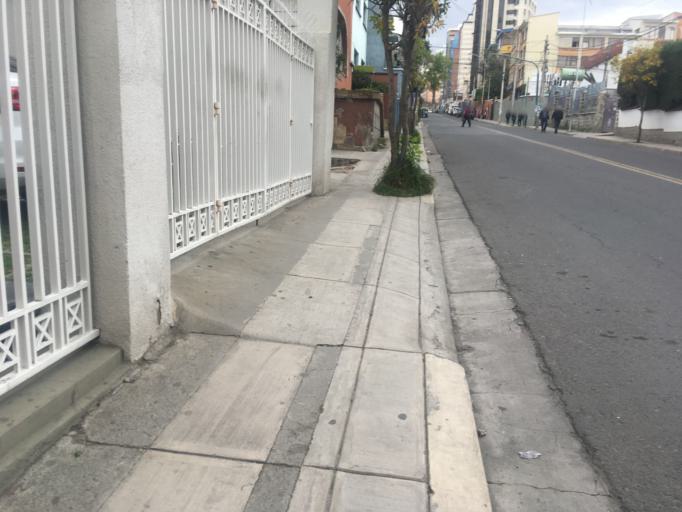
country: BO
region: La Paz
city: La Paz
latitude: -16.5072
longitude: -68.1252
